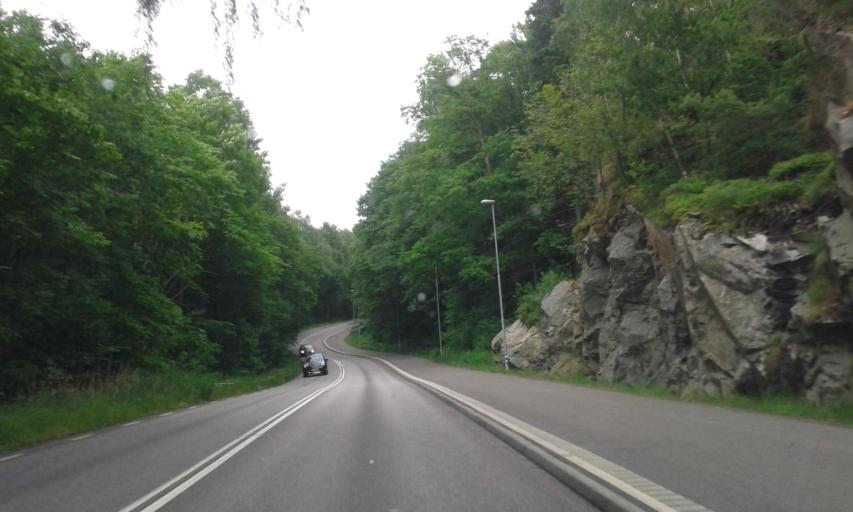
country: SE
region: Vaestra Goetaland
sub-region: Goteborg
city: Eriksbo
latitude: 57.7595
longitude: 12.0174
